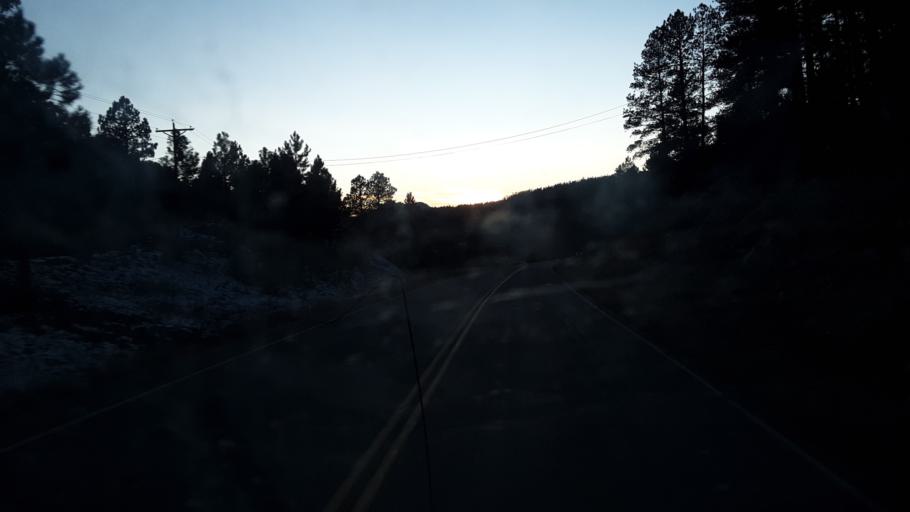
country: US
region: Colorado
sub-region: La Plata County
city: Durango
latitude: 37.3264
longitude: -107.7511
